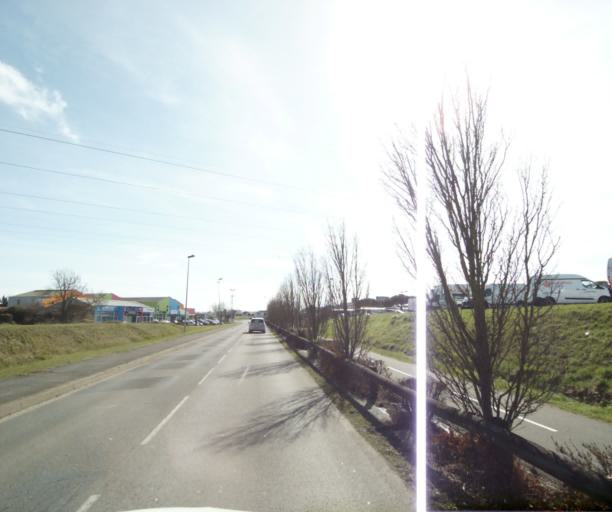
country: FR
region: Poitou-Charentes
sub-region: Departement de la Charente-Maritime
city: Lagord
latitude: 46.1759
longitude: -1.1671
